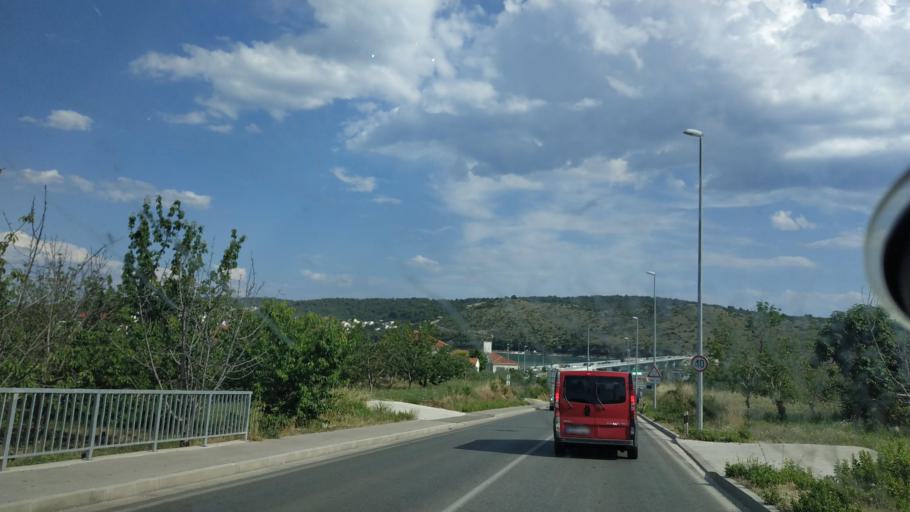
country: HR
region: Splitsko-Dalmatinska
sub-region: Grad Trogir
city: Trogir
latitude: 43.5244
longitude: 16.2635
